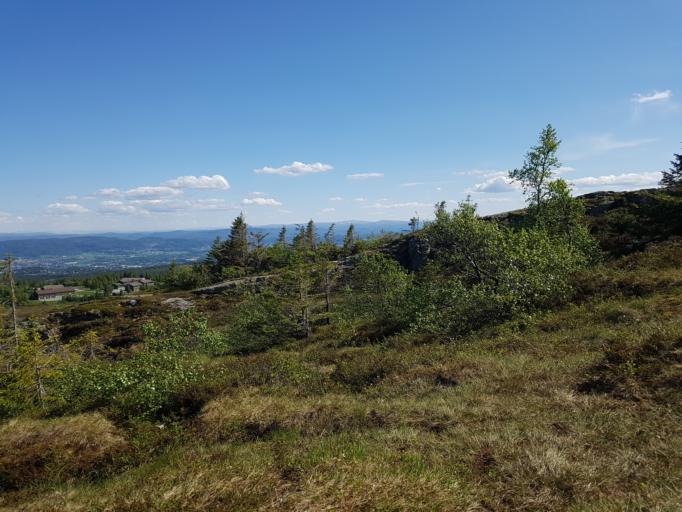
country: NO
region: Sor-Trondelag
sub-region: Melhus
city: Melhus
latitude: 63.4212
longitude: 10.2548
